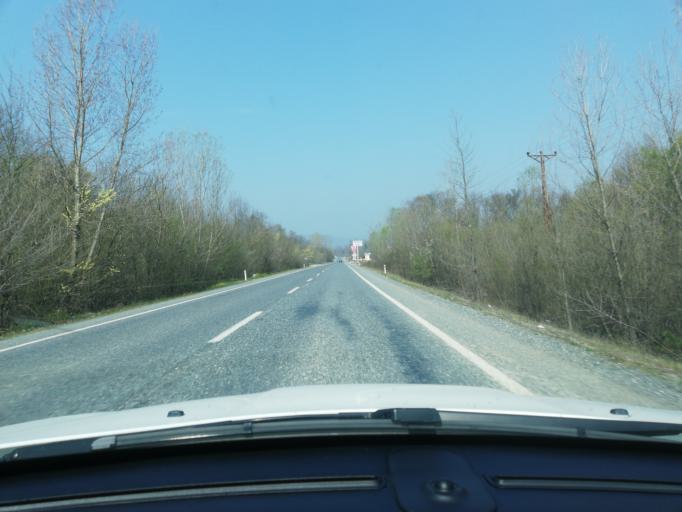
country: TR
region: Zonguldak
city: Gokcebey
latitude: 41.2939
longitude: 32.1315
